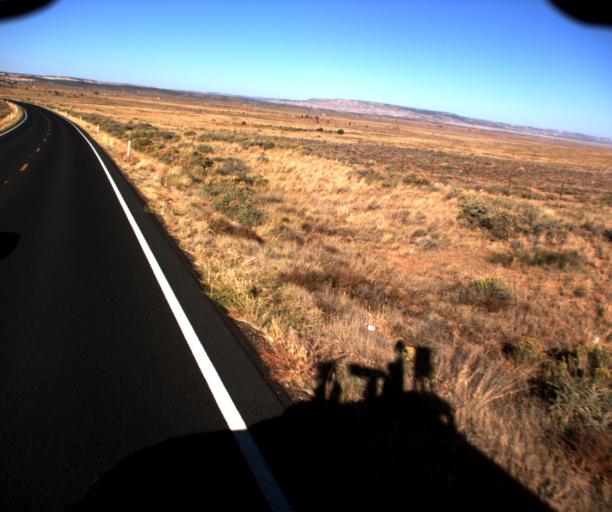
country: US
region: Arizona
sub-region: Apache County
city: Ganado
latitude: 35.7882
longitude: -109.6789
